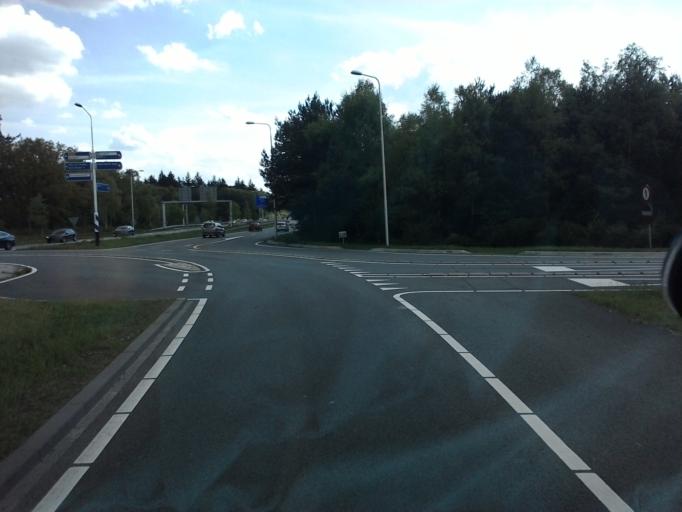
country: NL
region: Utrecht
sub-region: Gemeente Zeist
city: Zeist
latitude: 52.1088
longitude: 5.2614
